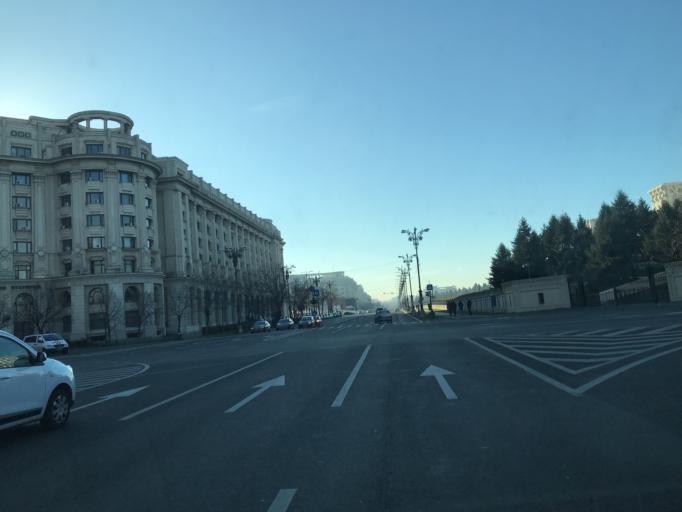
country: RO
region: Bucuresti
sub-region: Municipiul Bucuresti
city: Bucuresti
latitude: 44.4305
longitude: 26.0910
